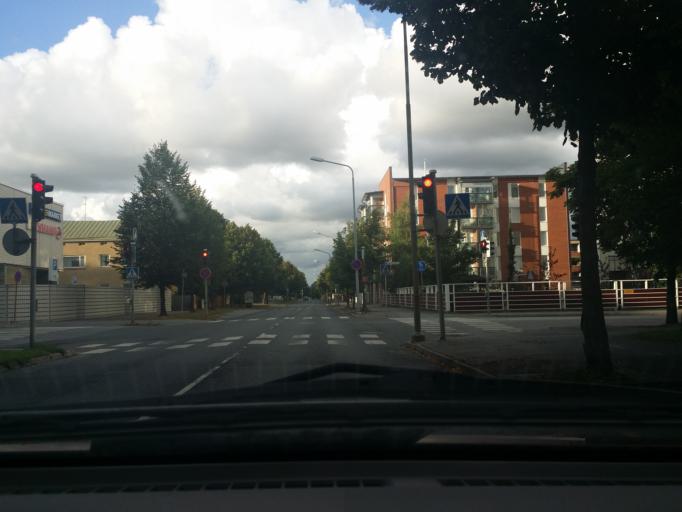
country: FI
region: Satakunta
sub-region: Pori
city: Pori
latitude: 61.4847
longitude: 21.8014
